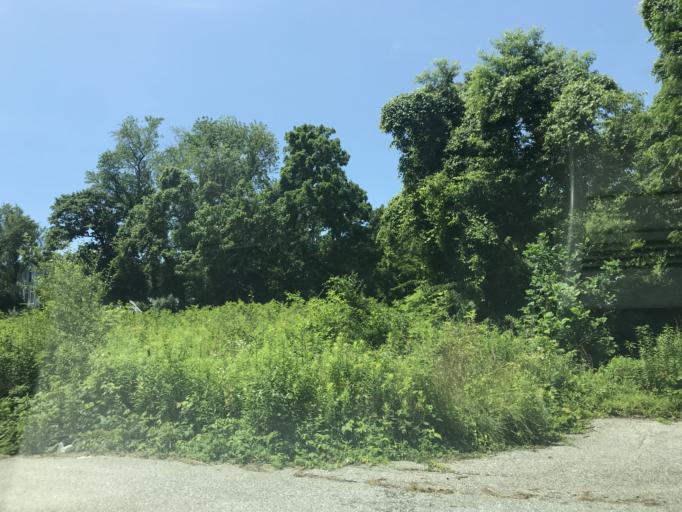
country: US
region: Maryland
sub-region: Harford County
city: South Bel Air
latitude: 39.5648
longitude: -76.2702
